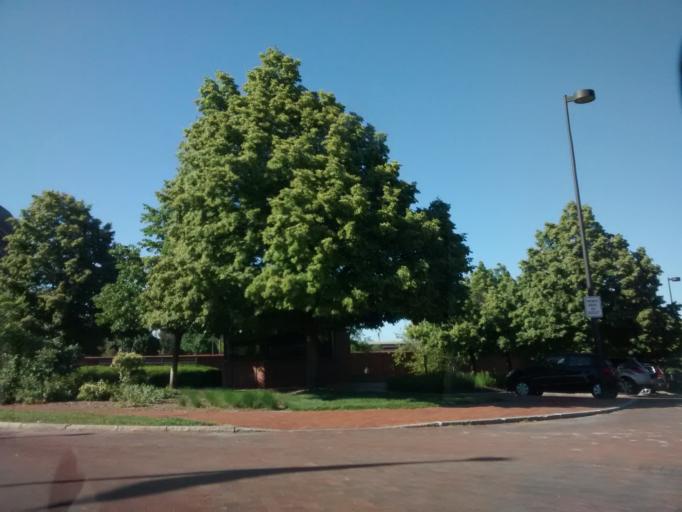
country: US
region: Nebraska
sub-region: Douglas County
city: Omaha
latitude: 41.2564
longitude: -95.9277
